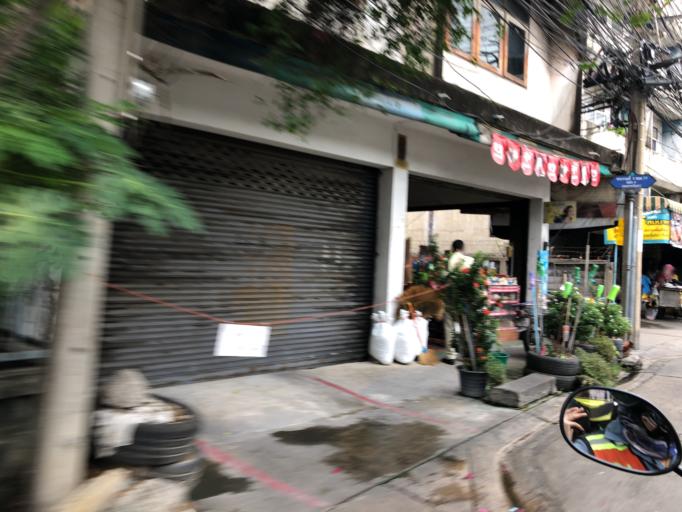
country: TH
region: Bangkok
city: Yan Nawa
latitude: 13.7114
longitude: 100.5500
